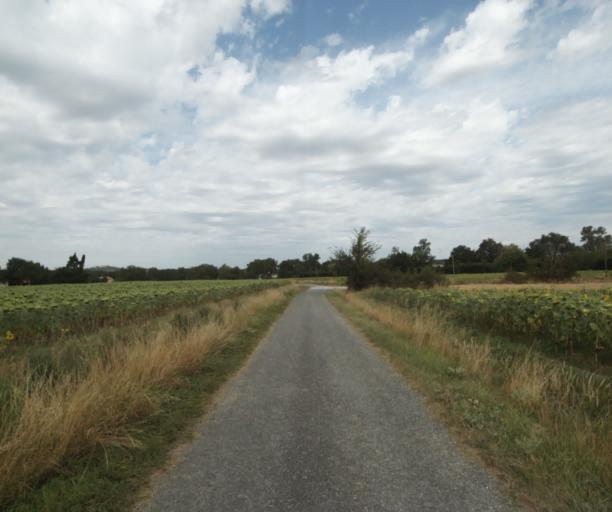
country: FR
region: Midi-Pyrenees
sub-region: Departement de la Haute-Garonne
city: Saint-Felix-Lauragais
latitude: 43.4460
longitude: 1.9364
